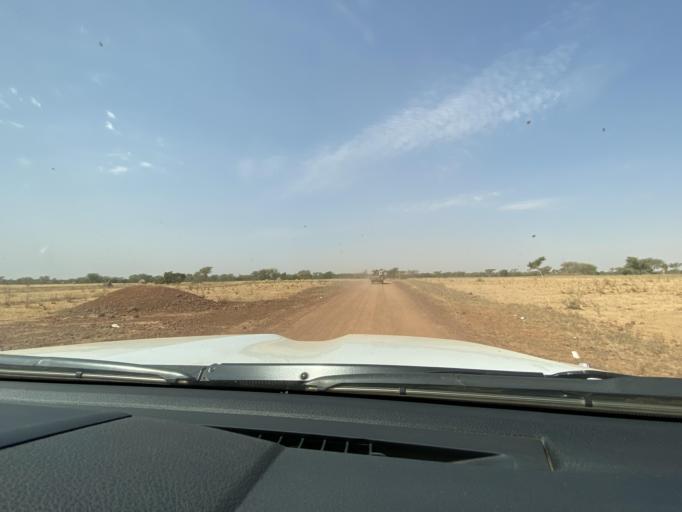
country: NE
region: Dosso
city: Birnin Gaoure
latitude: 13.2443
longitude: 2.8631
